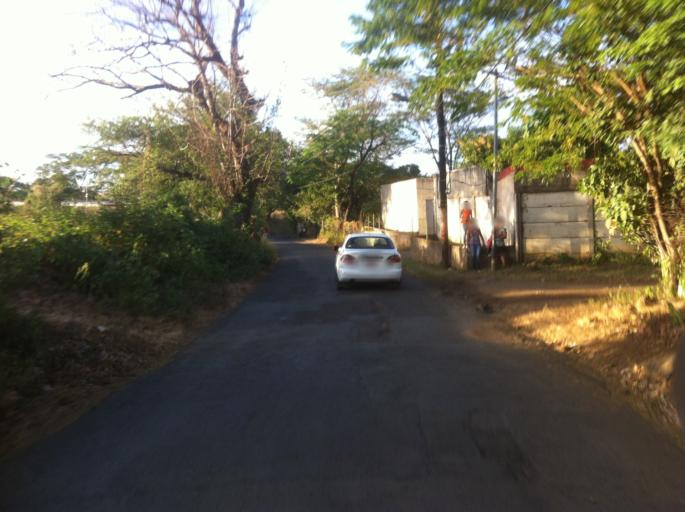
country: NI
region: Managua
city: Ciudad Sandino
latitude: 12.1069
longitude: -86.3135
